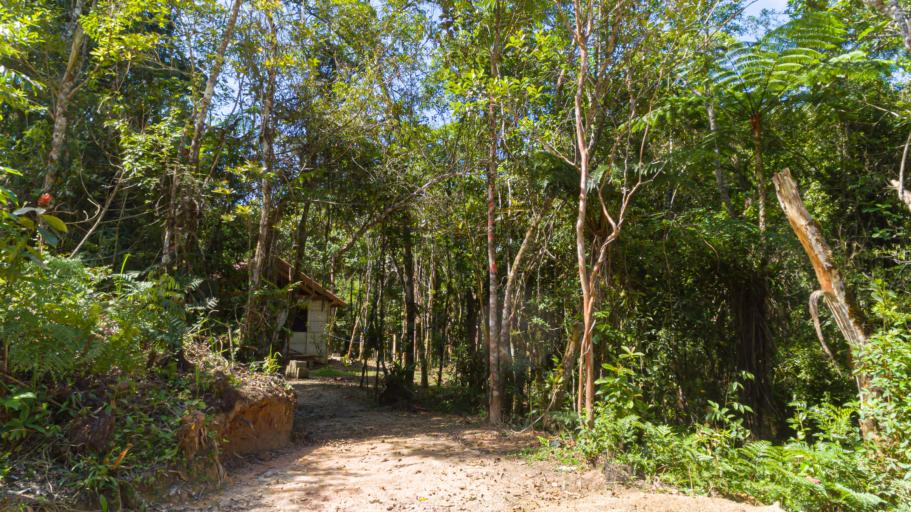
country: BR
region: Sao Paulo
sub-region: Juquitiba
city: Juquitiba
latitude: -24.0362
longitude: -47.2503
